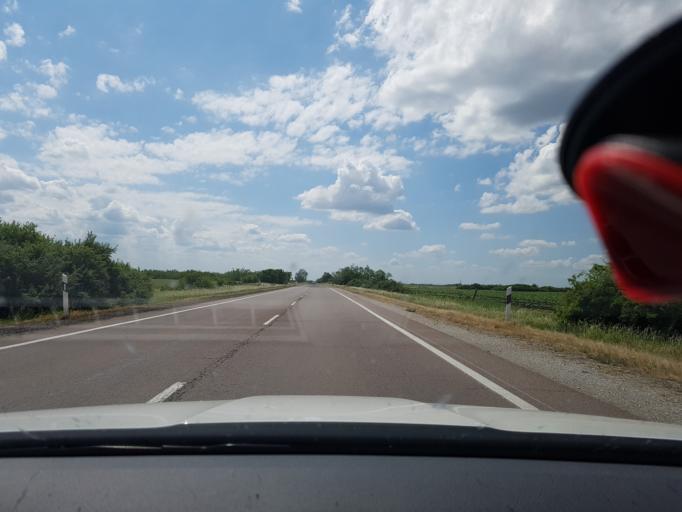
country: HU
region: Heves
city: Kompolt
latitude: 47.7595
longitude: 20.1930
